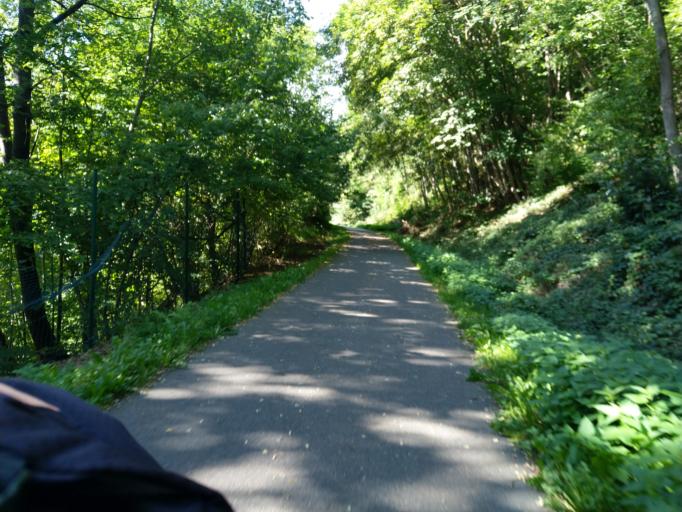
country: BE
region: Wallonia
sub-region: Province de Liege
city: Malmedy
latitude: 50.4190
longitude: 5.9997
